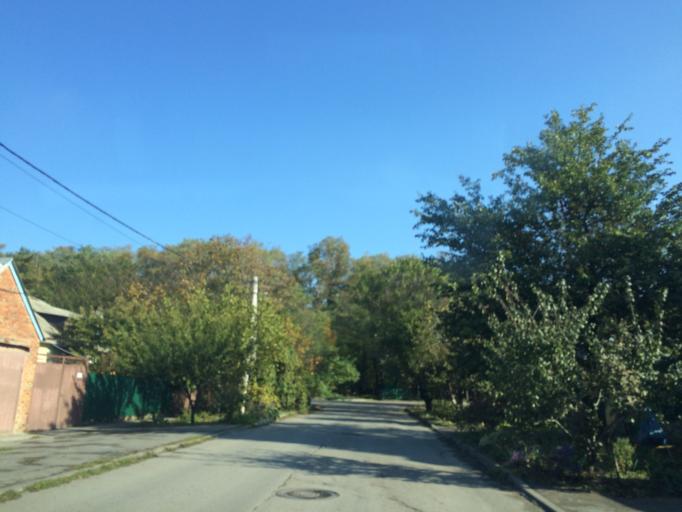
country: RU
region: Rostov
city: Imeni Chkalova
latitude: 47.2734
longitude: 39.7957
